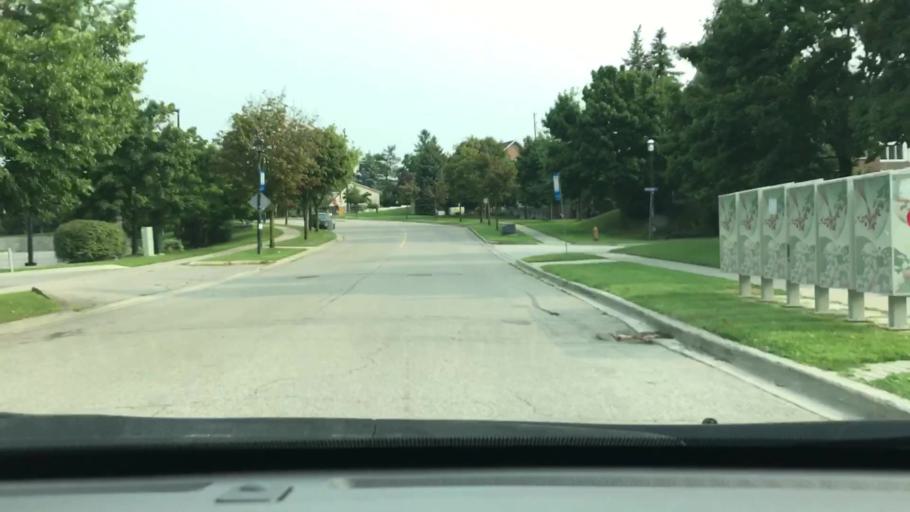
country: CA
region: Ontario
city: Newmarket
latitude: 44.0548
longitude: -79.4322
